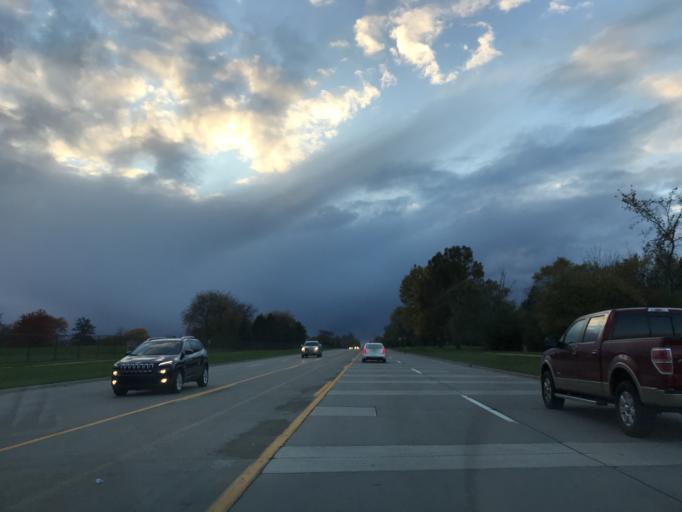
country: US
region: Michigan
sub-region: Oakland County
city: Farmington
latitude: 42.4398
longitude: -83.4067
